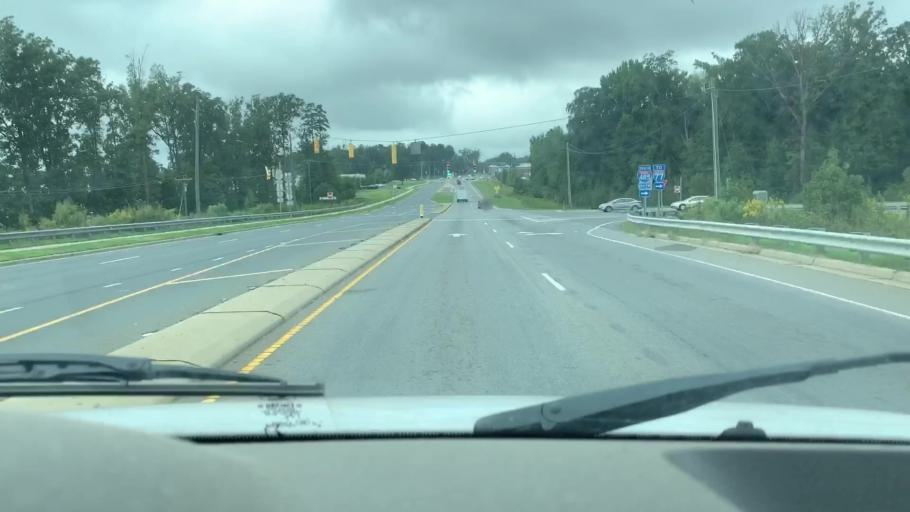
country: US
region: North Carolina
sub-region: Mecklenburg County
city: Huntersville
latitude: 35.3664
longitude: -80.8280
